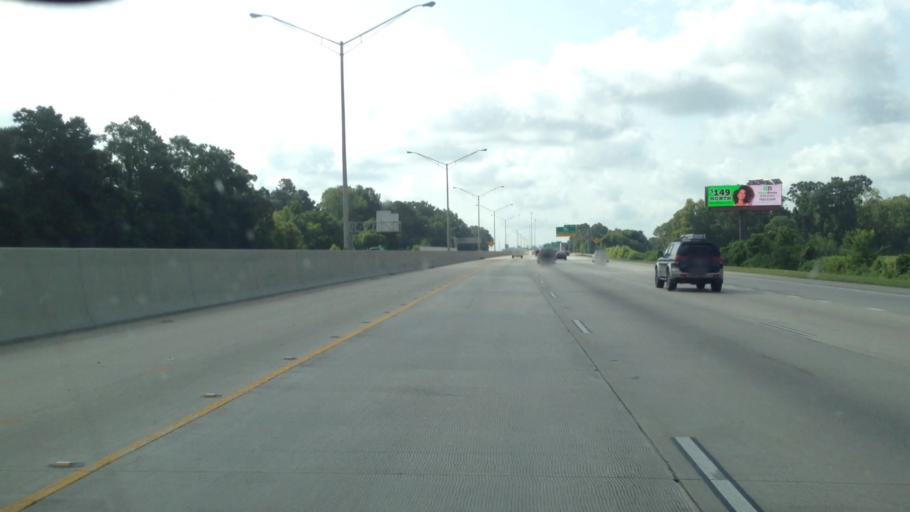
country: US
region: Louisiana
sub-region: East Baton Rouge Parish
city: Inniswold
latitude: 30.4032
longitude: -91.0959
